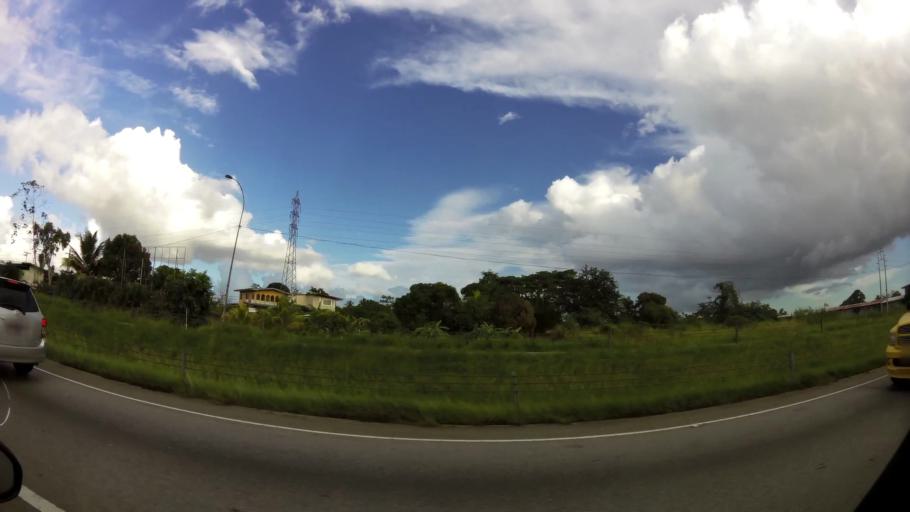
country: TT
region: Chaguanas
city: Chaguanas
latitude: 10.4584
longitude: -61.4105
